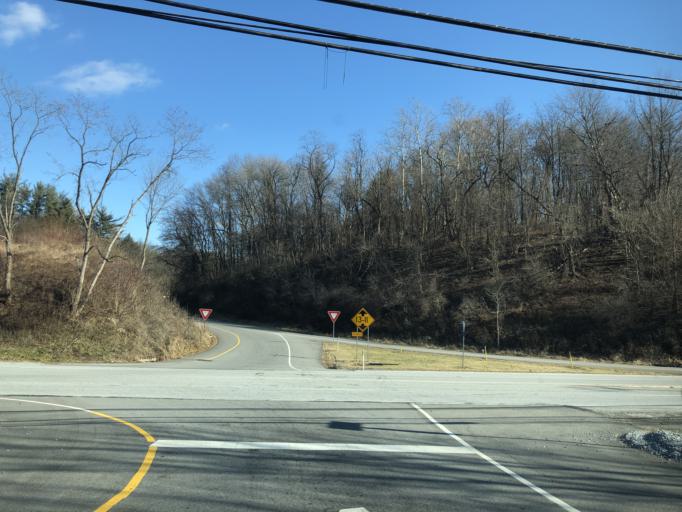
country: US
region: Pennsylvania
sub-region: Chester County
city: Coatesville
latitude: 40.0005
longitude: -75.8217
